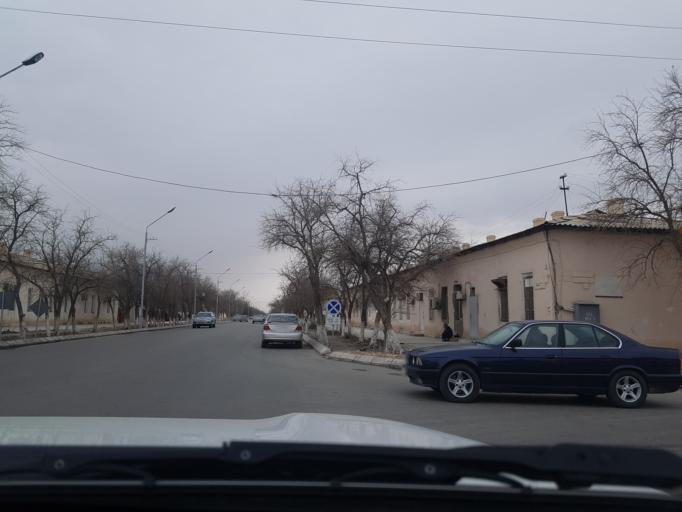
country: TM
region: Balkan
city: Balkanabat
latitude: 39.5051
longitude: 54.3610
